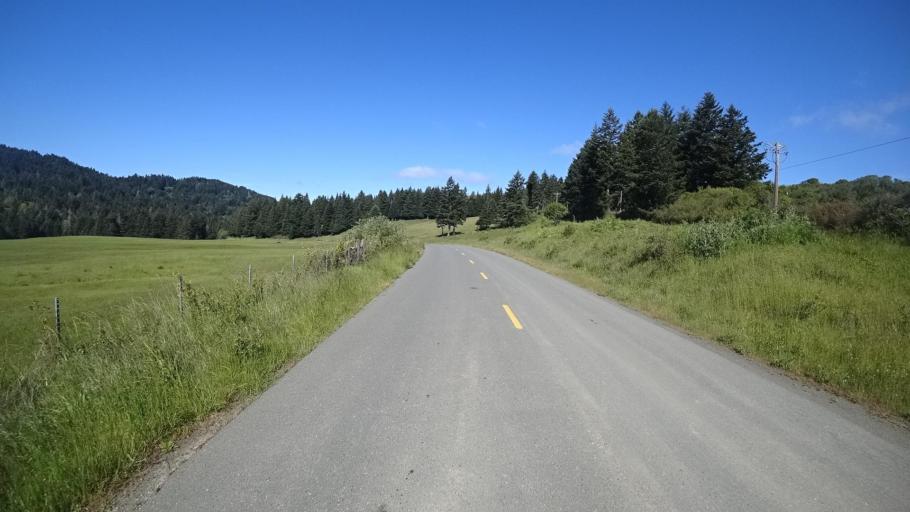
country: US
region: California
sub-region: Humboldt County
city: Ferndale
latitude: 40.3477
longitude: -124.3305
